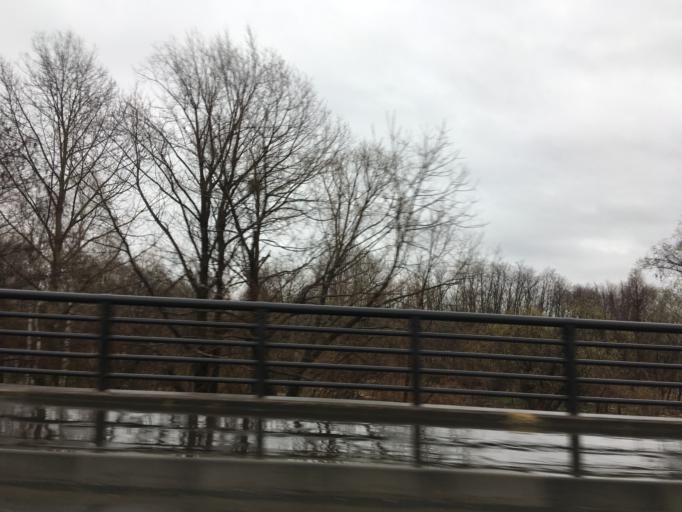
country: JP
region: Hokkaido
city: Nayoro
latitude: 44.1276
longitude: 142.4844
